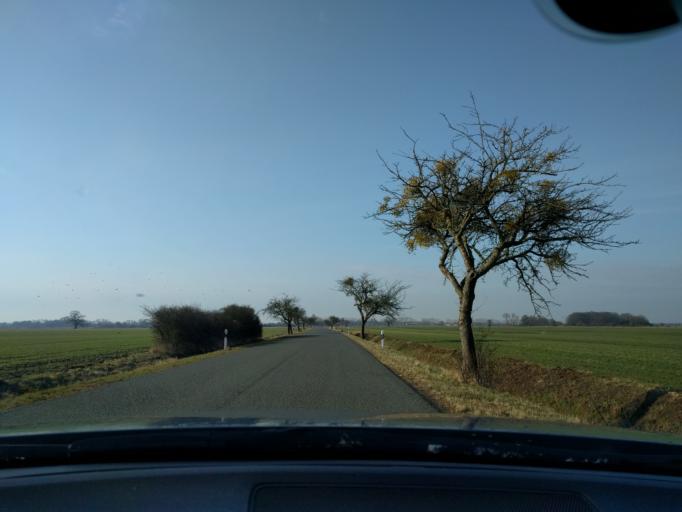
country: DE
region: Saxony-Anhalt
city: Iden
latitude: 52.7750
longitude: 11.9448
